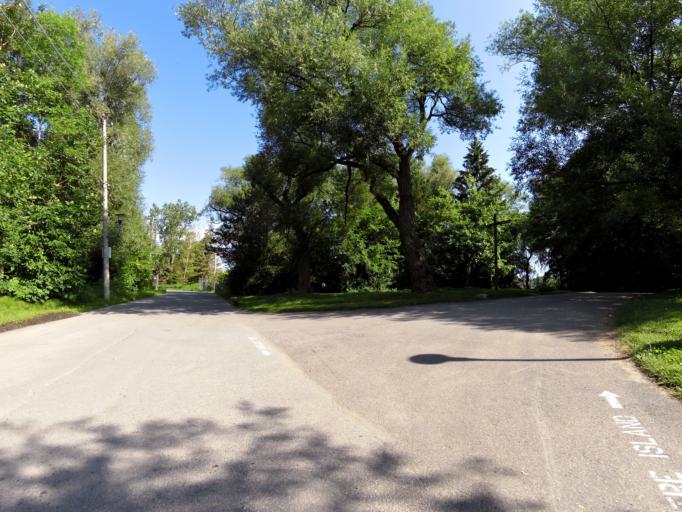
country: CA
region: Ontario
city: Toronto
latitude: 43.6156
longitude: -79.3798
